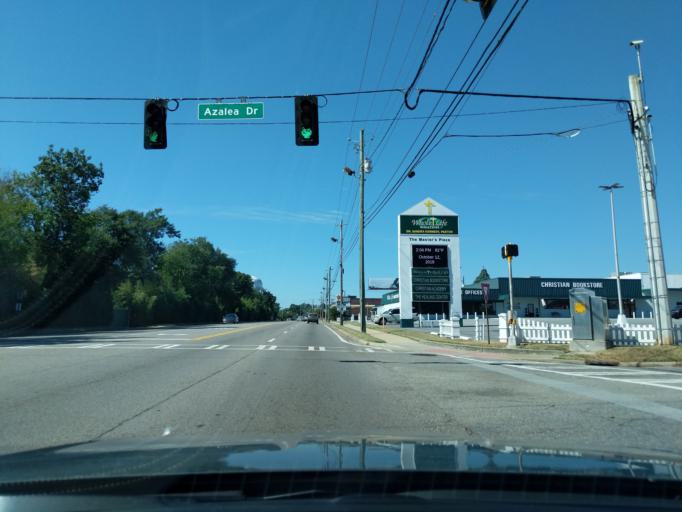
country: US
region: South Carolina
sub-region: Aiken County
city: North Augusta
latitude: 33.5065
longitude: -82.0192
